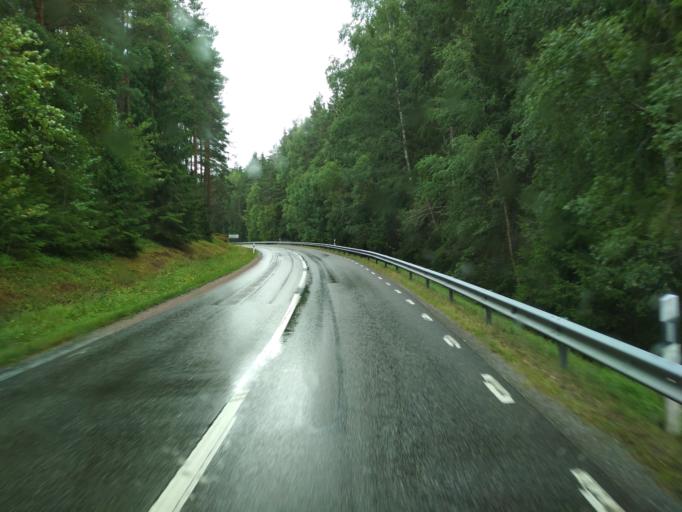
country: SE
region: Vaestmanland
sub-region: Surahammars Kommun
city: Ramnas
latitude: 59.7491
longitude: 16.2070
